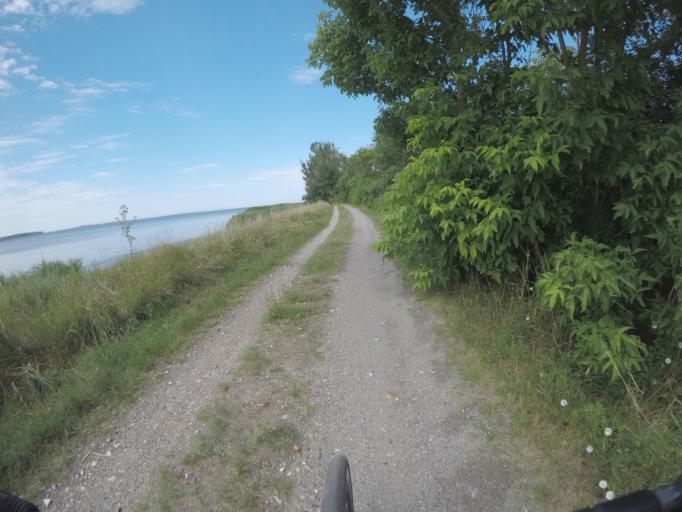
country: DE
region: Mecklenburg-Vorpommern
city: Altefahr
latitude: 54.3600
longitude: 13.1231
